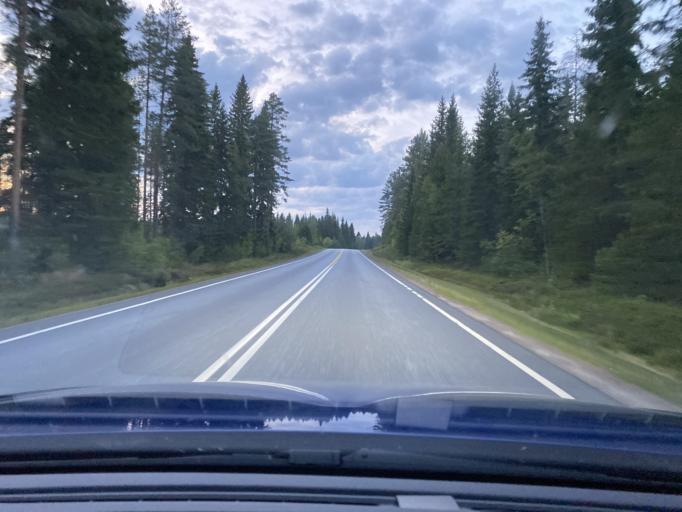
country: FI
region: Southern Ostrobothnia
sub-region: Suupohja
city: Kauhajoki
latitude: 62.2478
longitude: 22.2728
